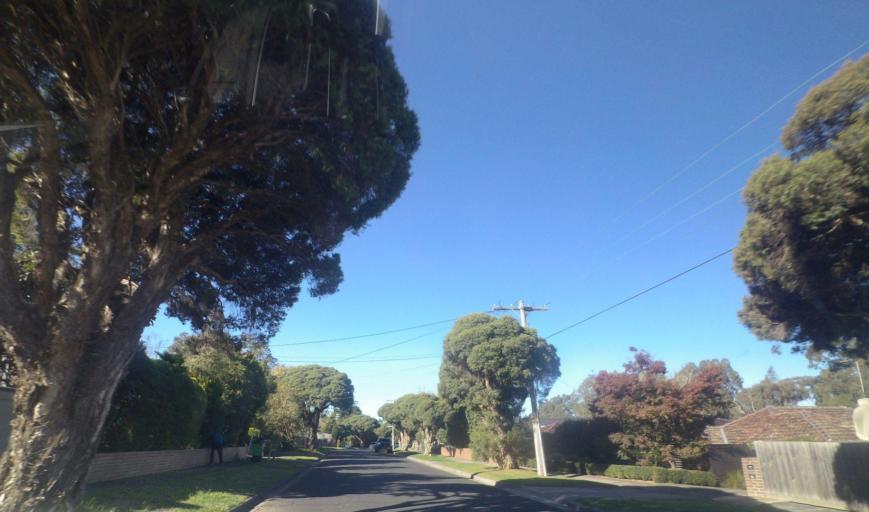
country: AU
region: Victoria
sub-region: Whitehorse
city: Box Hill North
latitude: -37.8057
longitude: 145.1282
